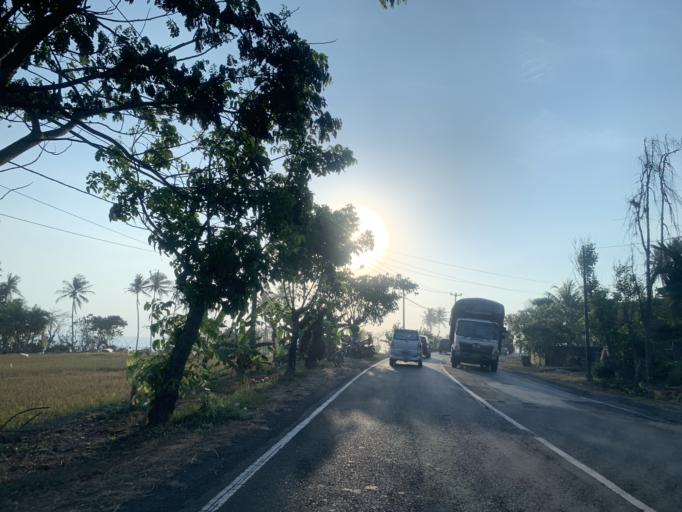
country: ID
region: Bali
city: Angkahgede
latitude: -8.4780
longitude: 114.9376
